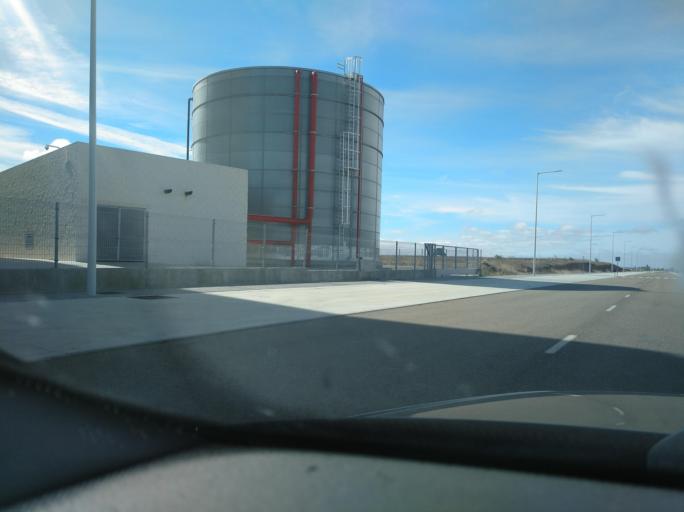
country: ES
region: Extremadura
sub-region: Provincia de Badajoz
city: Badajoz
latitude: 38.9157
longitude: -7.0067
